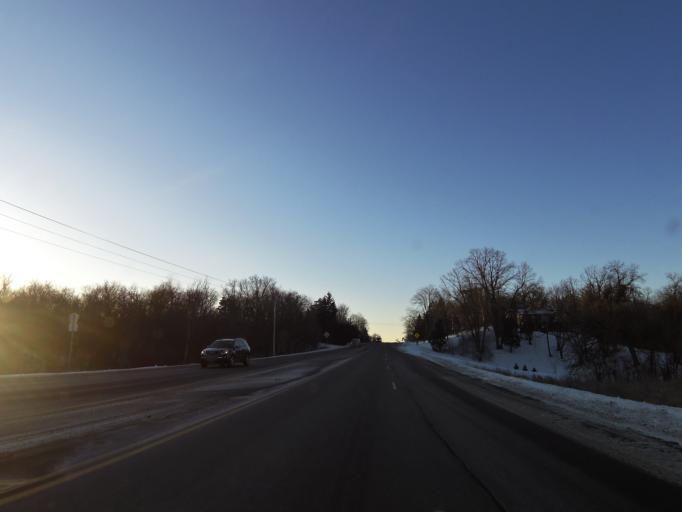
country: US
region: Minnesota
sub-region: Scott County
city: Prior Lake
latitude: 44.7163
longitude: -93.3792
